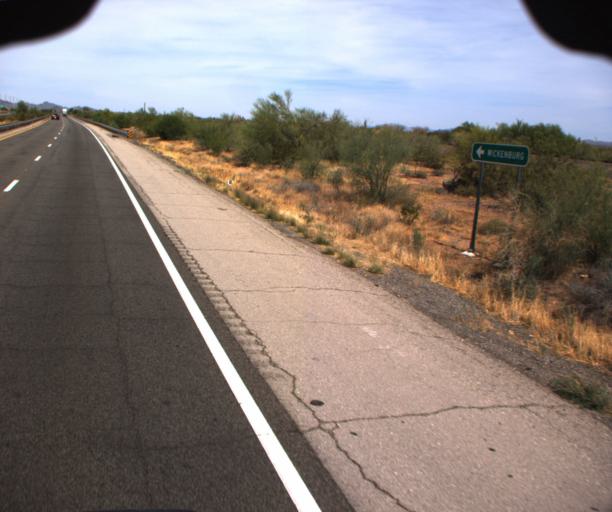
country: US
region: Arizona
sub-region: Maricopa County
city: Wickenburg
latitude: 33.8284
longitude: -112.5933
